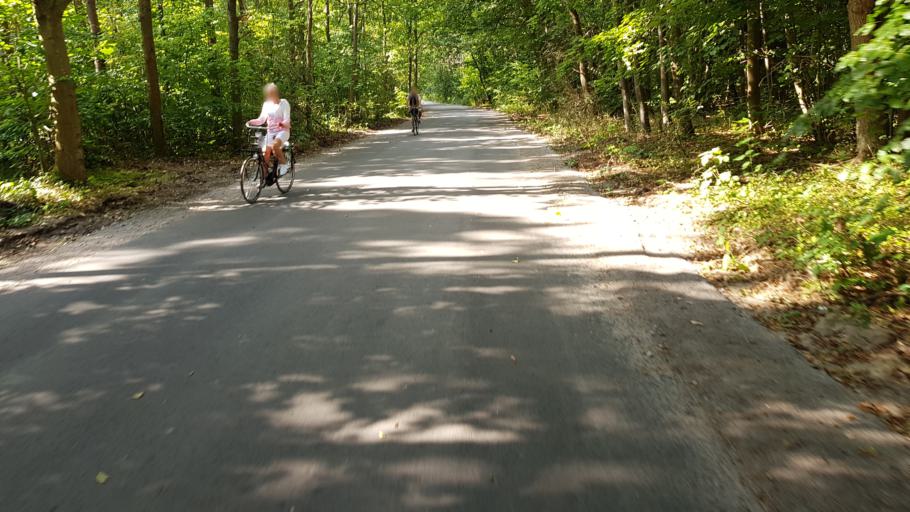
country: PL
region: West Pomeranian Voivodeship
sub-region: Powiat slawienski
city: Darlowo
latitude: 54.5148
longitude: 16.4802
